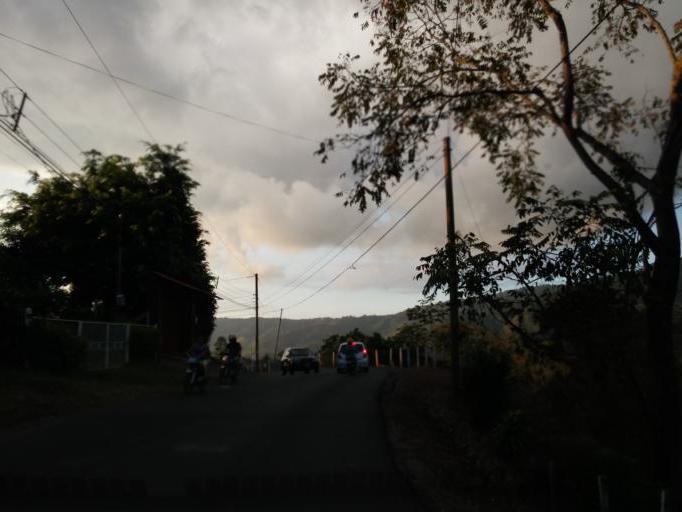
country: CR
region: San Jose
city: Palmichal
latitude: 9.8405
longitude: -84.2133
